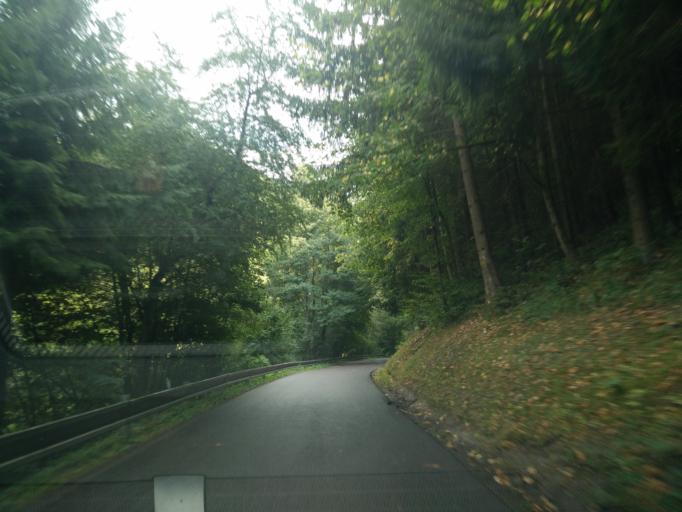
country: SK
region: Banskobystricky
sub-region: Okres Banska Bystrica
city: Banska Stiavnica
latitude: 48.4972
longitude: 18.8309
